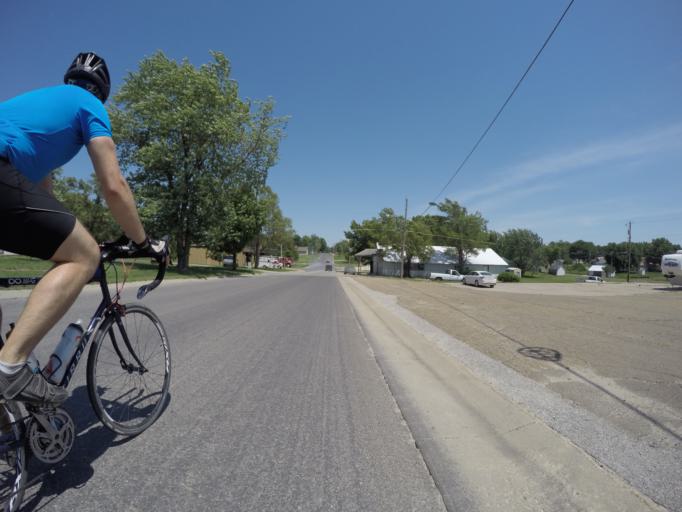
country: US
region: Kansas
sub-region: Nemaha County
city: Sabetha
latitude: 39.8998
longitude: -95.8064
